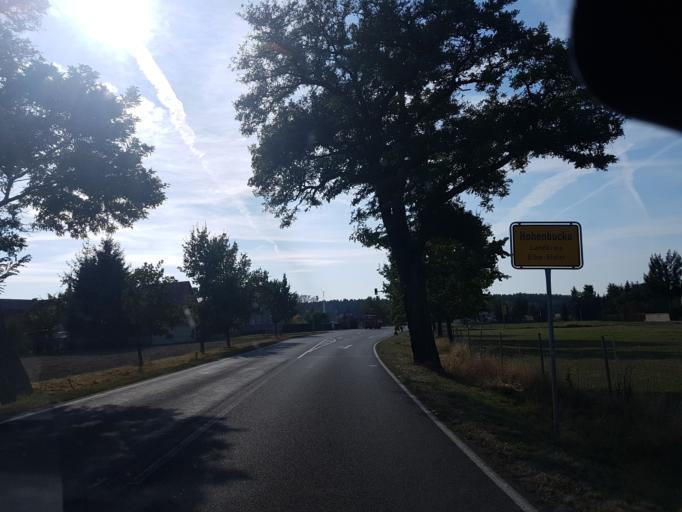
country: DE
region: Brandenburg
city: Hohenbucko
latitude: 51.7644
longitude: 13.4724
